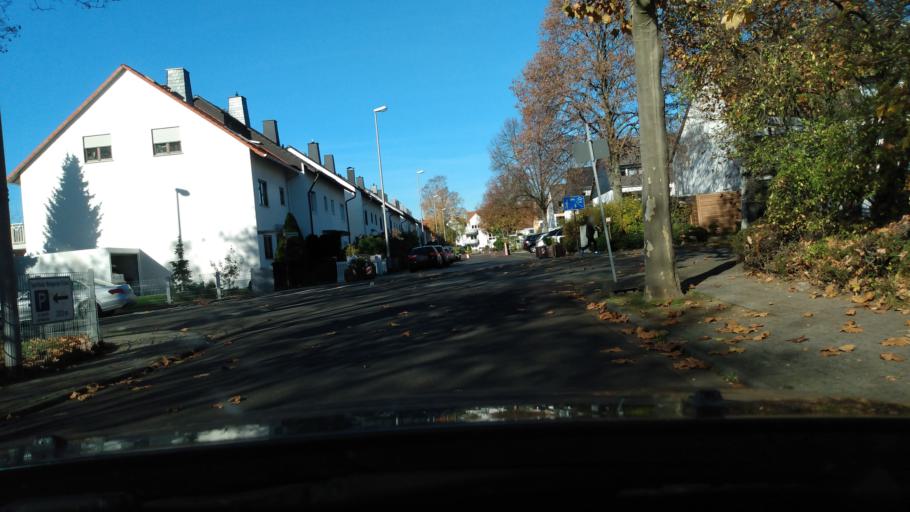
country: DE
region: Hesse
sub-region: Regierungsbezirk Darmstadt
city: Kriftel
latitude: 50.0879
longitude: 8.4677
